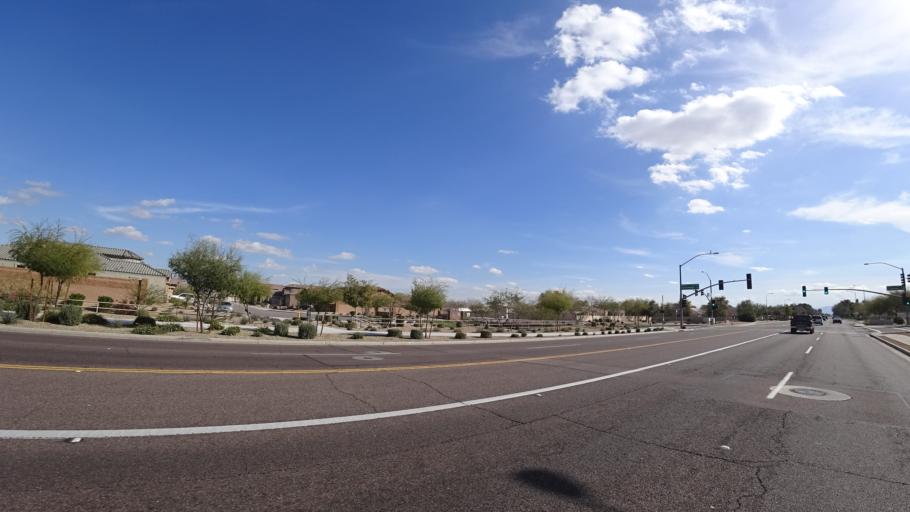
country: US
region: Arizona
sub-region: Maricopa County
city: Peoria
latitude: 33.6255
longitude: -112.2201
